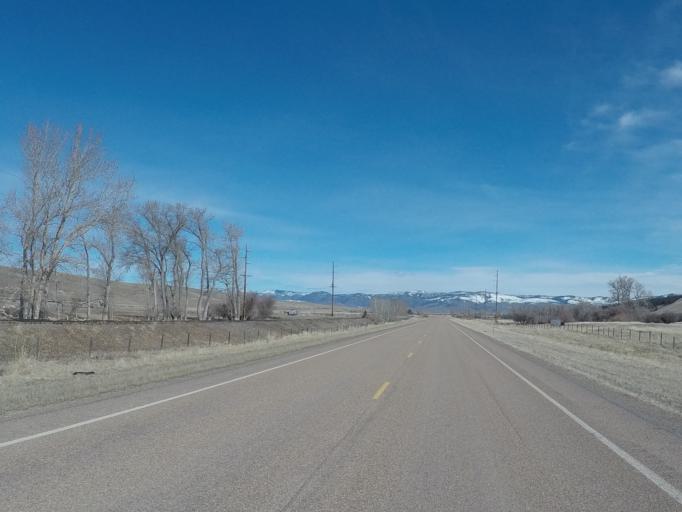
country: US
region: Montana
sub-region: Granite County
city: Philipsburg
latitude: 46.5381
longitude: -113.2214
